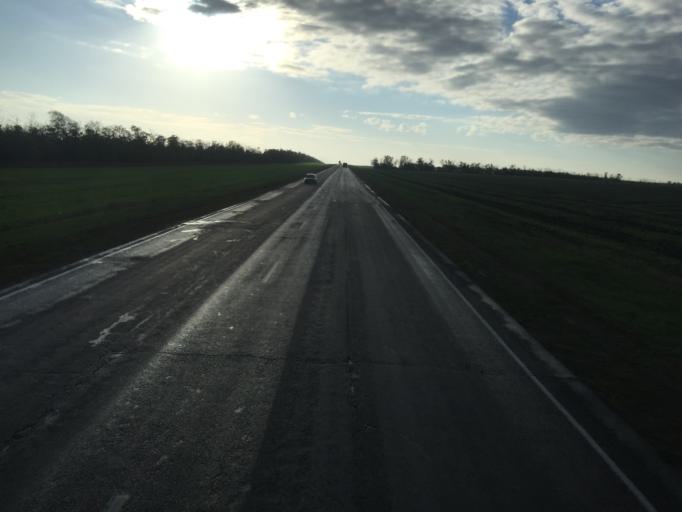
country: RU
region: Rostov
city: Kagal'nitskaya
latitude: 46.8676
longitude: 40.1730
